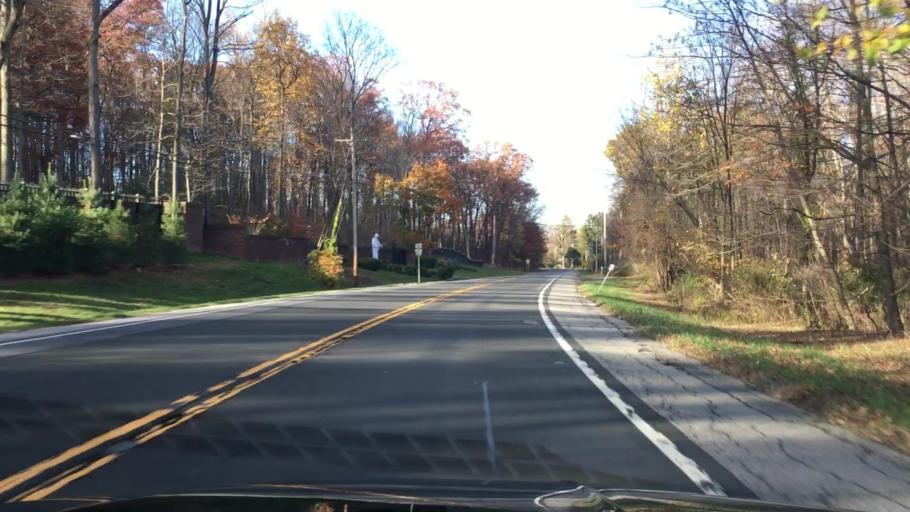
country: US
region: New York
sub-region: Dutchess County
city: Myers Corner
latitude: 41.6099
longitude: -73.8488
